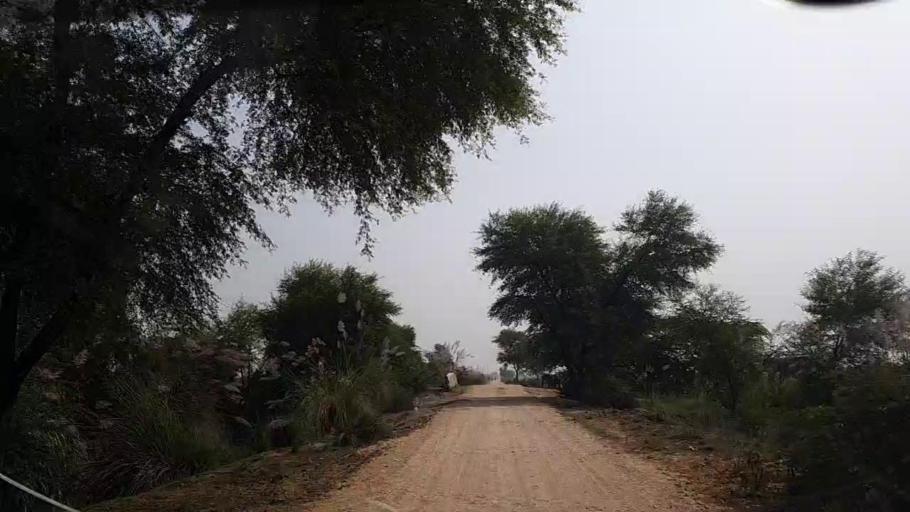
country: PK
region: Sindh
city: Garhi Yasin
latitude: 27.9301
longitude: 68.5586
